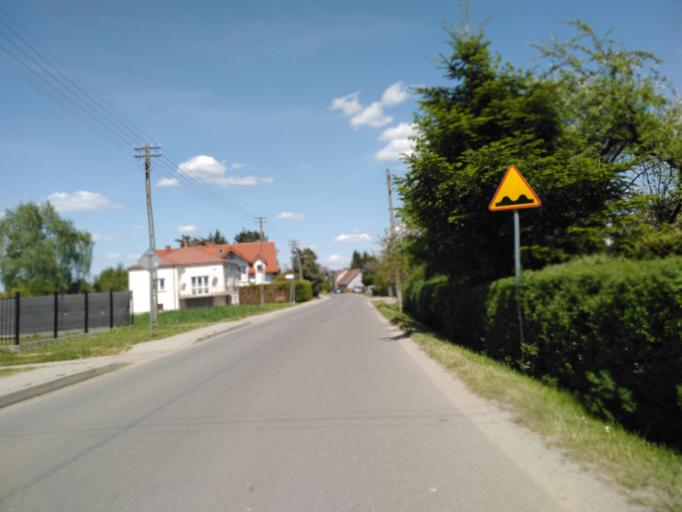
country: PL
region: Subcarpathian Voivodeship
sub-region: Powiat krosnienski
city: Odrzykon
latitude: 49.7135
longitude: 21.7069
